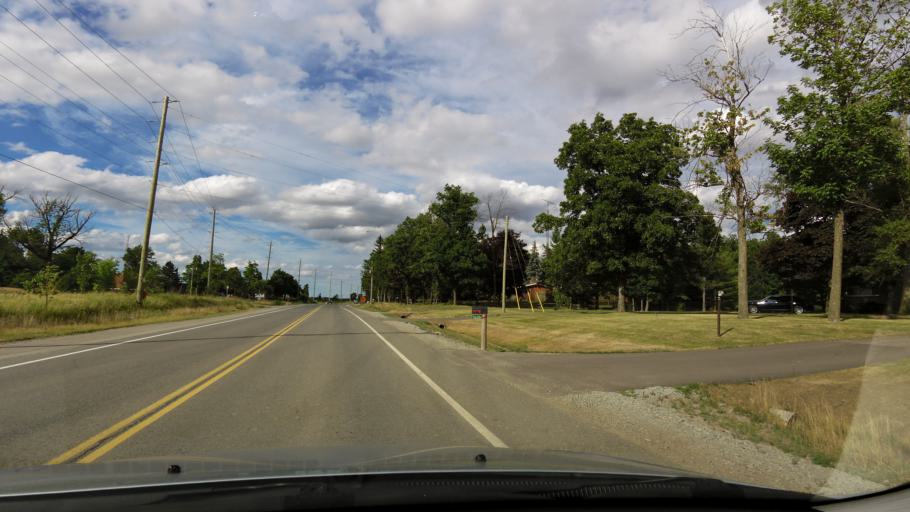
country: CA
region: Ontario
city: Brampton
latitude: 43.6990
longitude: -79.8626
